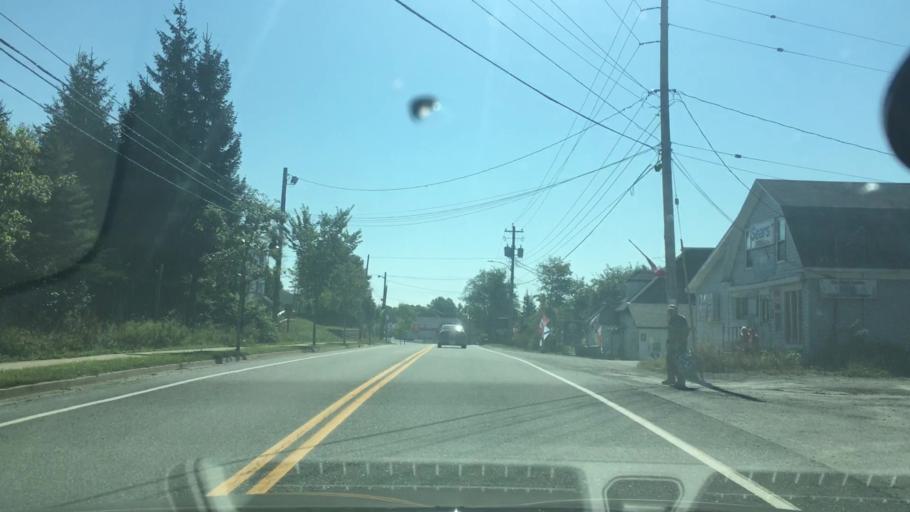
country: CA
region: Nova Scotia
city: New Glasgow
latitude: 44.9257
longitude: -62.5412
